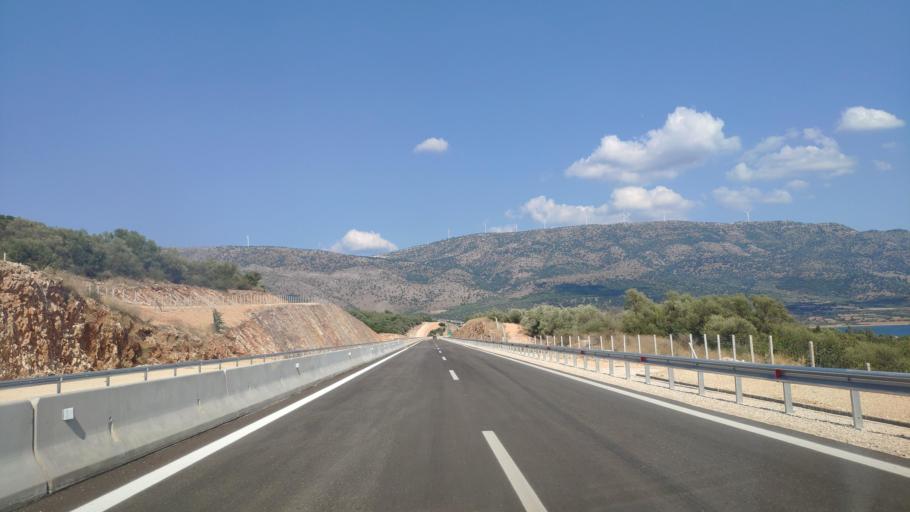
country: GR
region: West Greece
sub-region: Nomos Aitolias kai Akarnanias
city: Stanos
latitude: 38.7714
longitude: 21.1636
